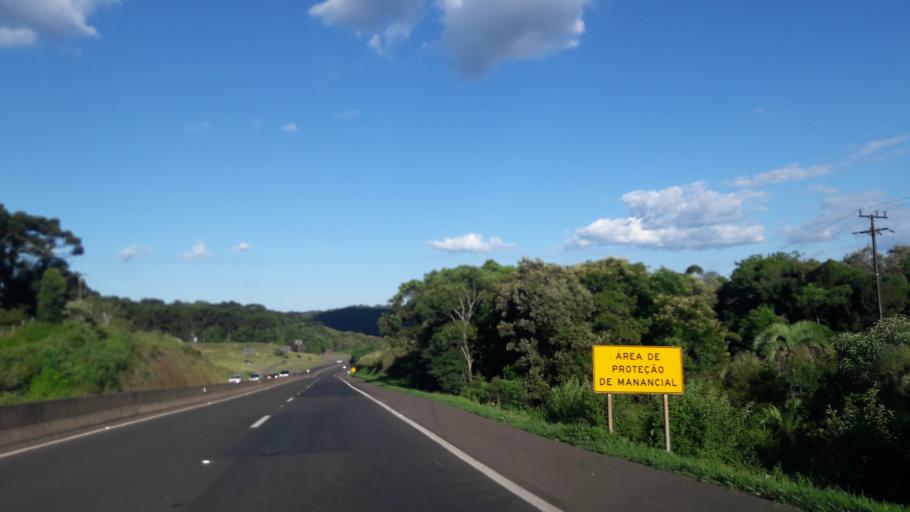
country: BR
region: Parana
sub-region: Guarapuava
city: Guarapuava
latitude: -25.3402
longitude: -51.4205
